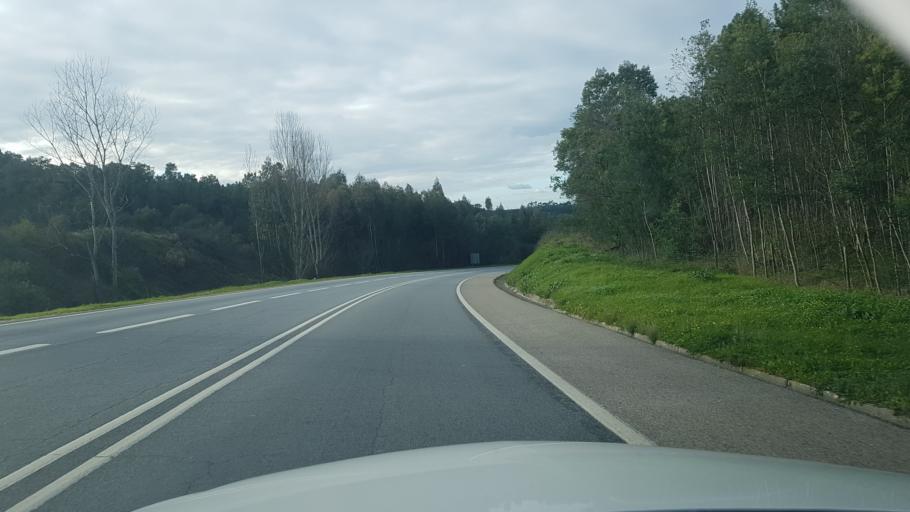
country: PT
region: Santarem
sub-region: Abrantes
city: Abrantes
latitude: 39.4646
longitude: -8.2204
